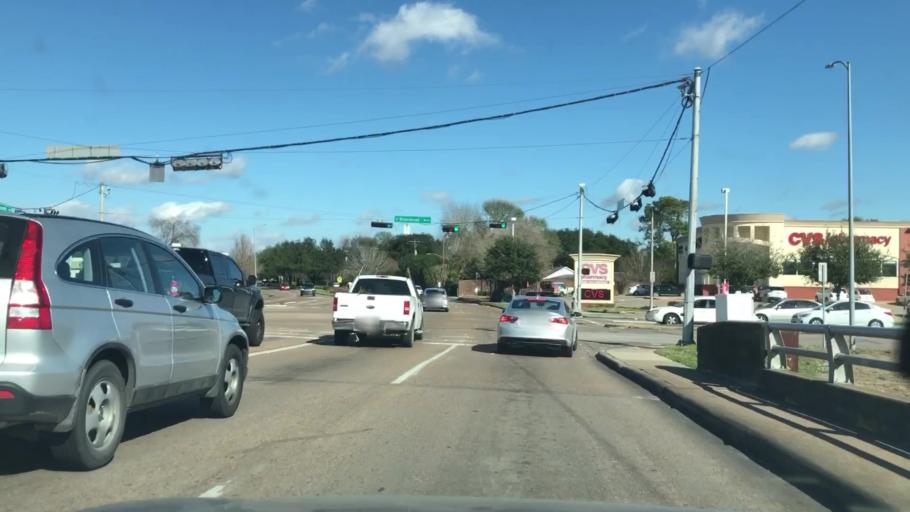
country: US
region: Texas
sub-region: Harris County
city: Bellaire
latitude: 29.6783
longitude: -95.4931
